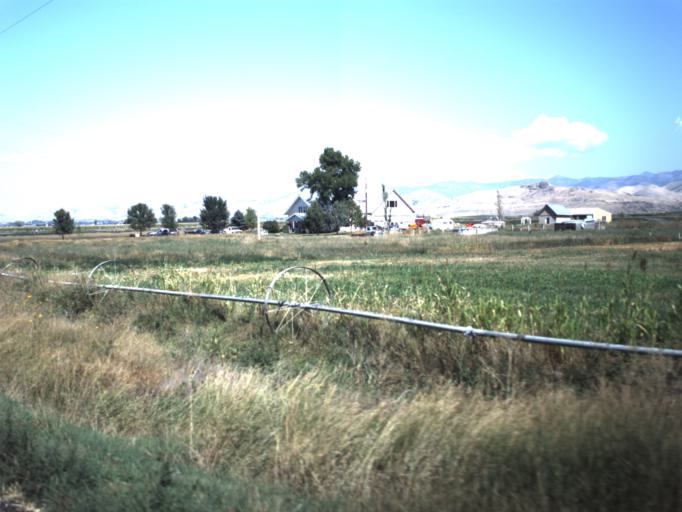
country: US
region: Utah
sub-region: Cache County
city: Lewiston
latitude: 41.9951
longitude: -111.8765
